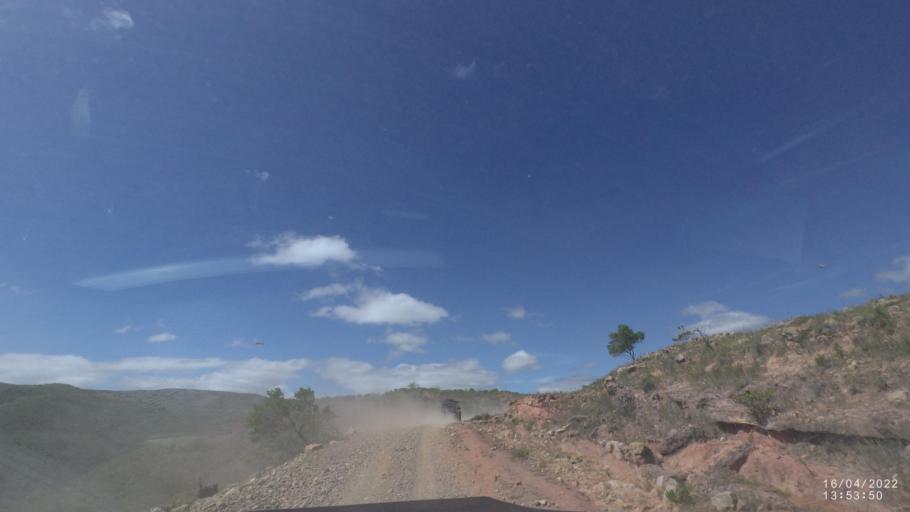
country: BO
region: Cochabamba
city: Mizque
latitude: -18.0252
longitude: -65.5691
